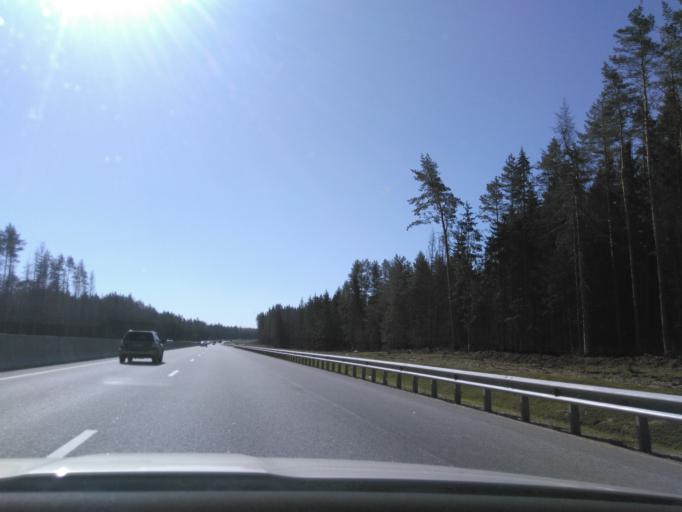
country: RU
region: Moskovskaya
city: Mendeleyevo
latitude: 56.0580
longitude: 37.2464
